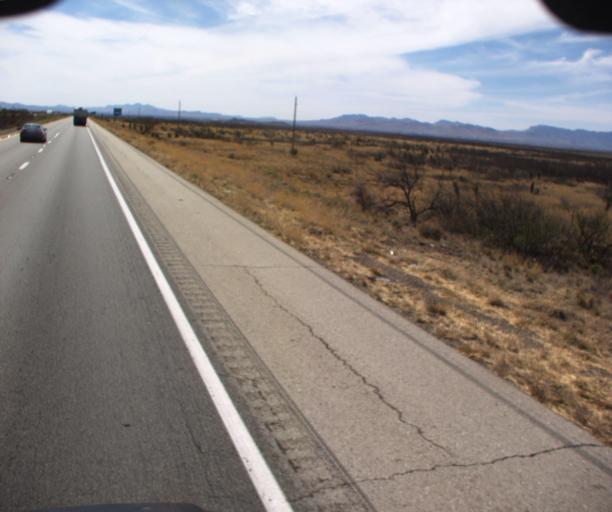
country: US
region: Arizona
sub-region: Cochise County
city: Willcox
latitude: 32.3287
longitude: -109.7708
